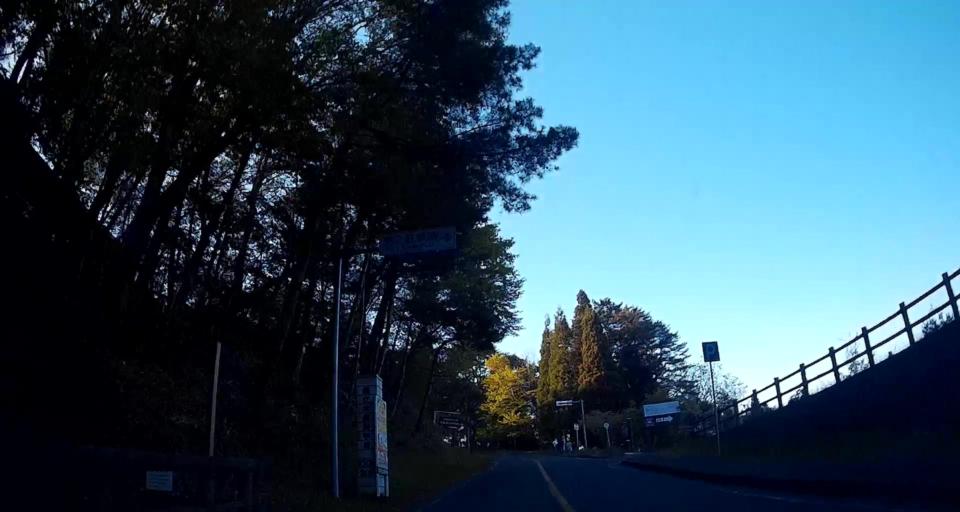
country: JP
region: Iwate
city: Miyako
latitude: 39.6482
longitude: 141.9770
